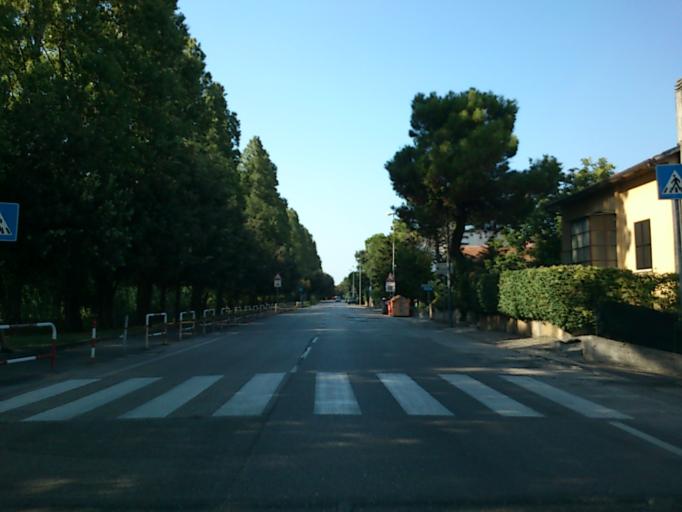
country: IT
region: The Marches
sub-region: Provincia di Pesaro e Urbino
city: Fano
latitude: 43.8320
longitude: 13.0144
